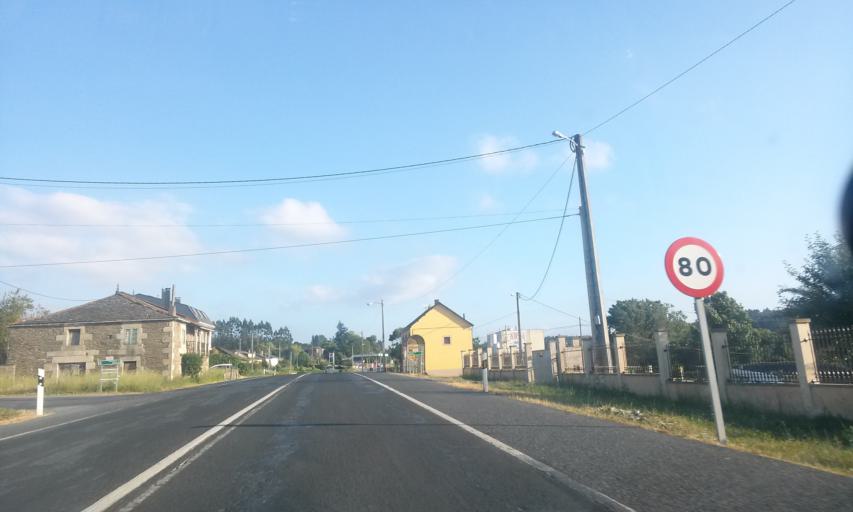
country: ES
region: Galicia
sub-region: Provincia de Lugo
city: Outeiro de Rei
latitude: 43.0875
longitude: -7.6062
